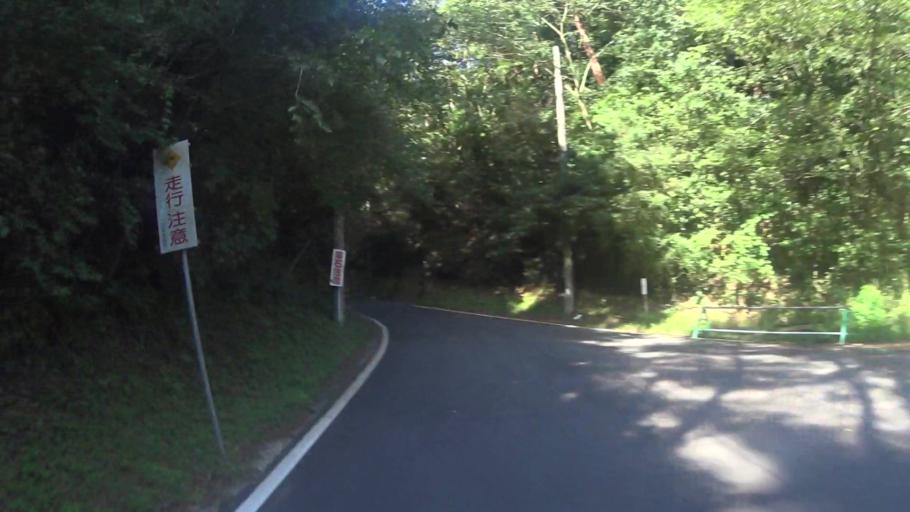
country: JP
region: Kyoto
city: Uji
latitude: 34.8127
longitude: 135.8916
